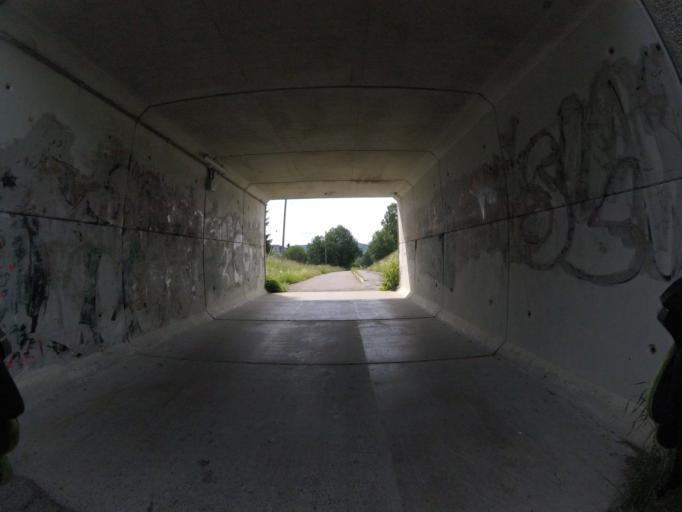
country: NO
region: Akershus
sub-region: Skedsmo
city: Lillestrom
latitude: 59.9728
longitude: 11.0553
